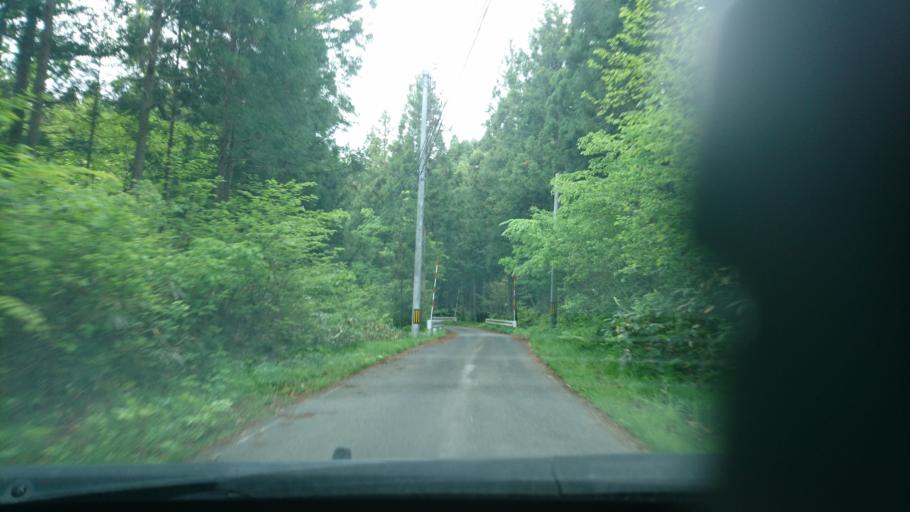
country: JP
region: Iwate
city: Ichinoseki
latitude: 38.9039
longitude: 140.9127
